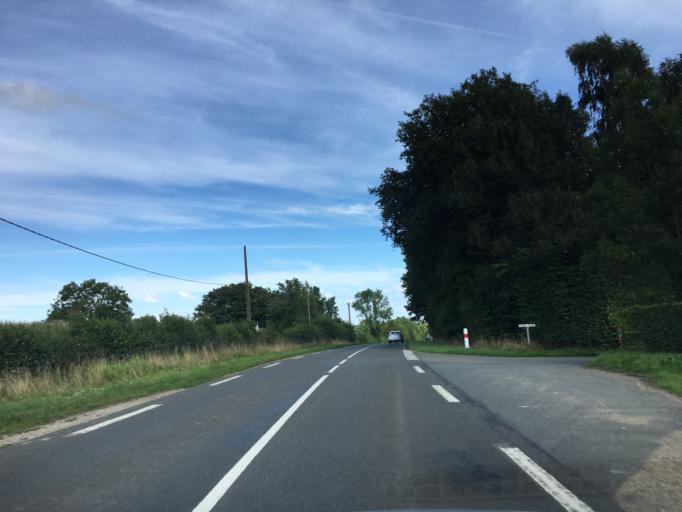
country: FR
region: Lower Normandy
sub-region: Departement du Calvados
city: Cambremer
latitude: 49.1416
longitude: 0.0925
